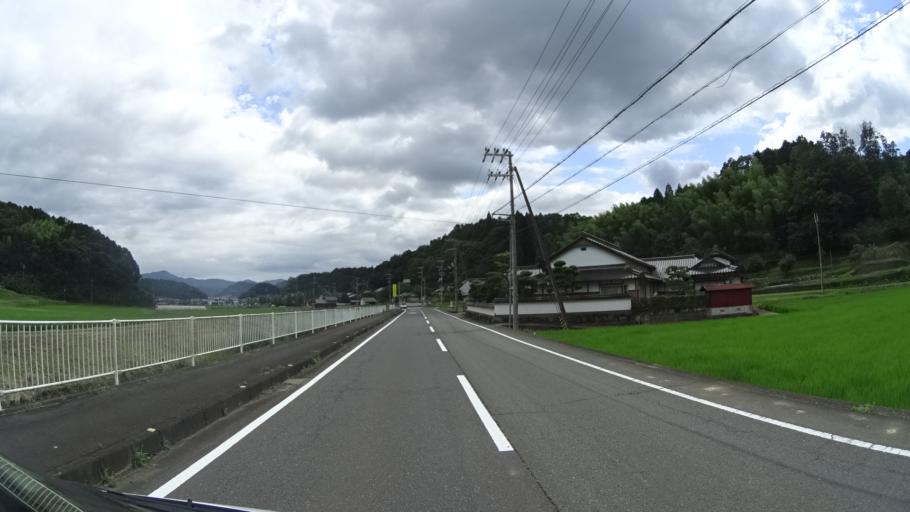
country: JP
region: Kyoto
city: Ayabe
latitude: 35.3266
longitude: 135.2627
